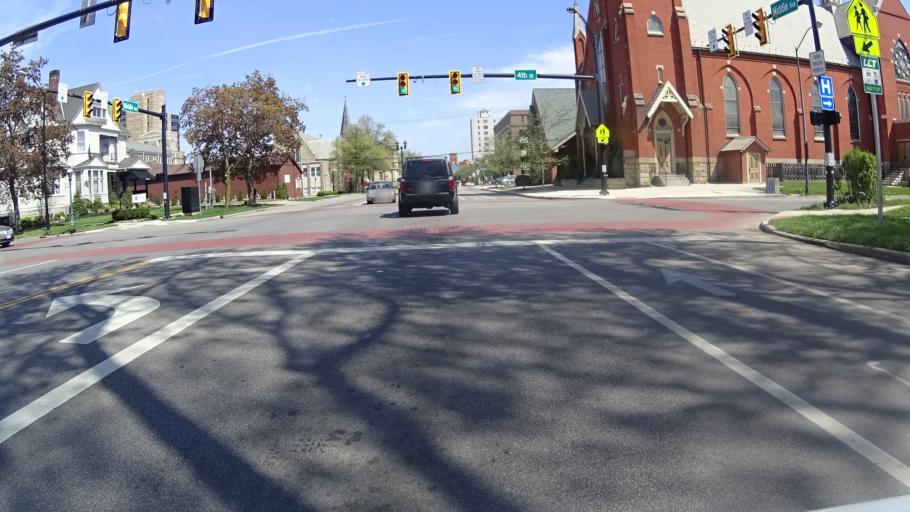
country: US
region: Ohio
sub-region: Lorain County
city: Elyria
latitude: 41.3640
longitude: -82.1071
